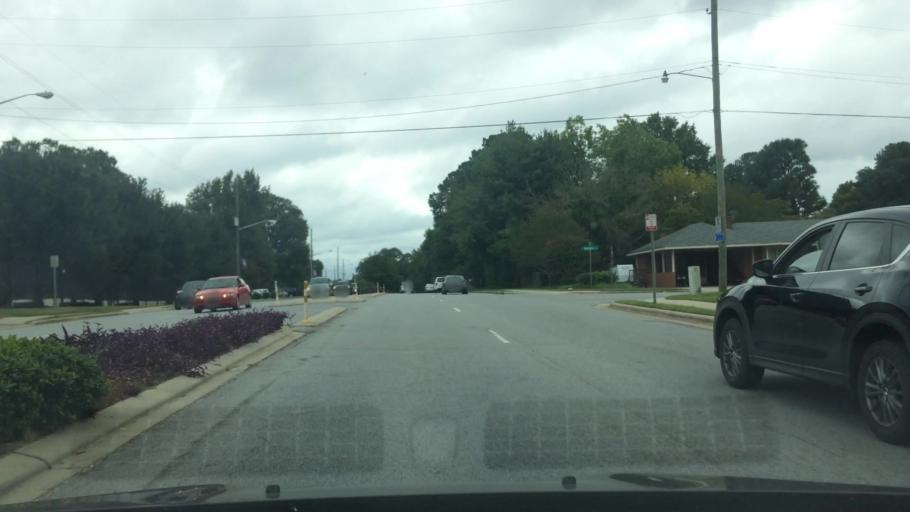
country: US
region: North Carolina
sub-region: Pitt County
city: Greenville
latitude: 35.5958
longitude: -77.3697
